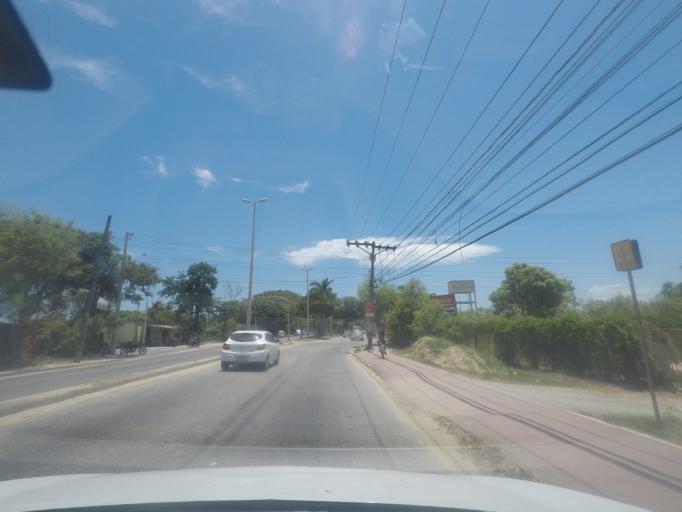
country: BR
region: Rio de Janeiro
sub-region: Itaguai
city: Itaguai
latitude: -22.9014
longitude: -43.6810
